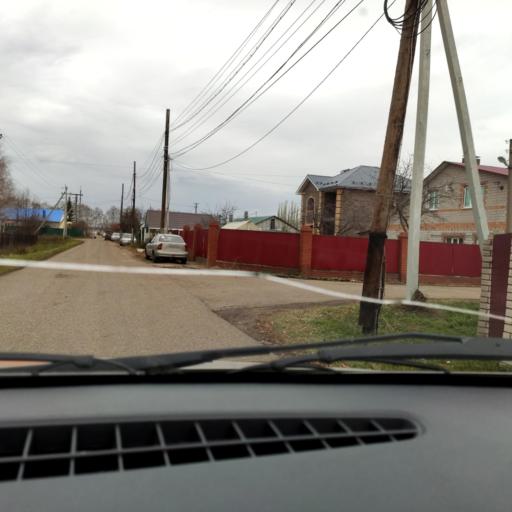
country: RU
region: Bashkortostan
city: Ufa
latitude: 54.8341
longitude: 56.0000
